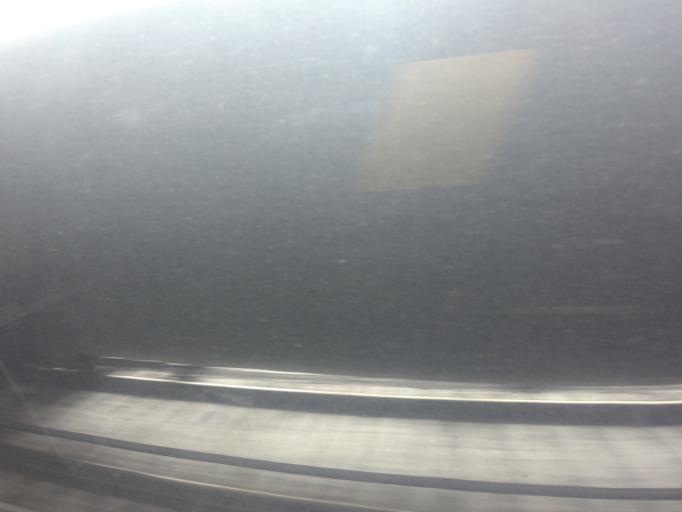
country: CA
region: Ontario
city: Quinte West
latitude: 44.0198
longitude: -77.7982
